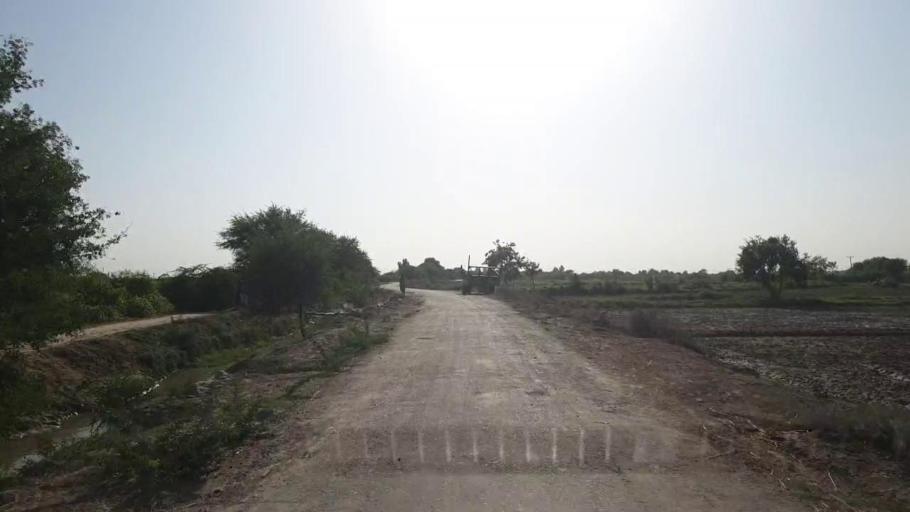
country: PK
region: Sindh
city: Badin
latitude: 24.6007
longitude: 68.9149
